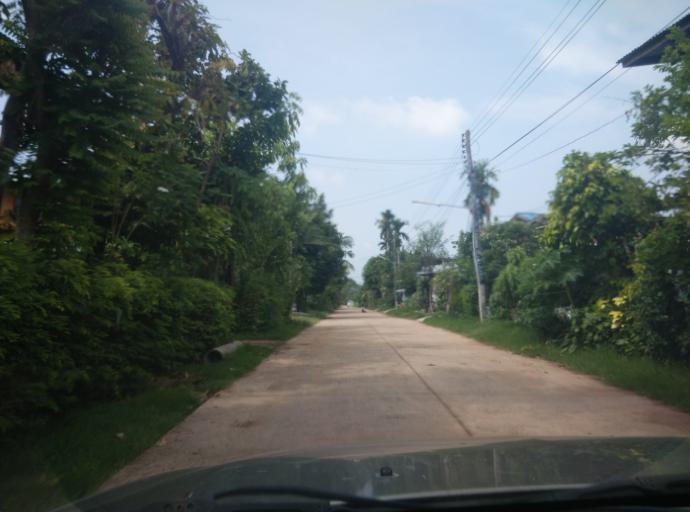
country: TH
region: Sisaket
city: Huai Thap Than
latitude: 15.0279
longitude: 104.0721
